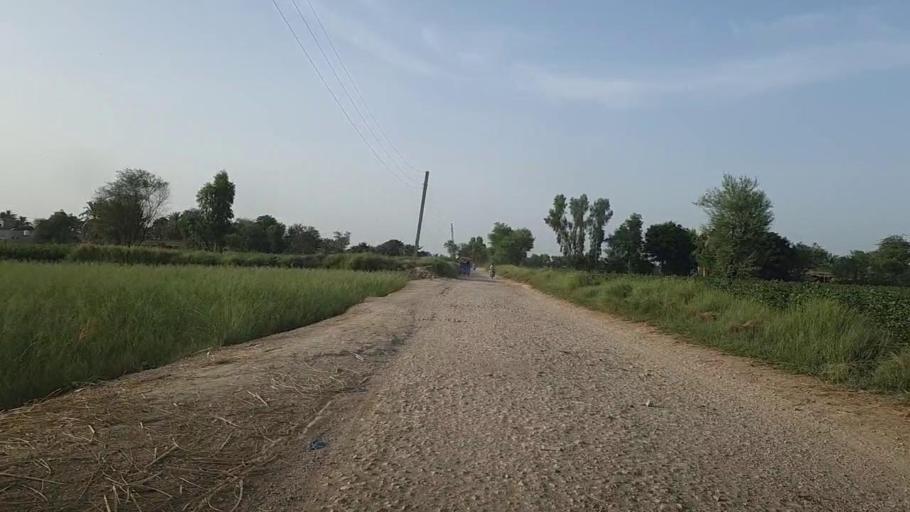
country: PK
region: Sindh
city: Bhiria
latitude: 26.8919
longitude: 68.2619
